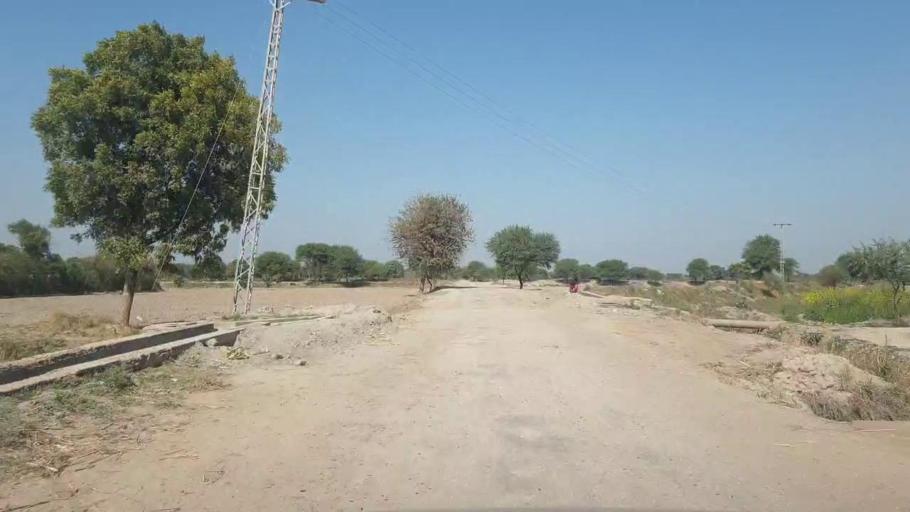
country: PK
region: Sindh
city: Chambar
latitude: 25.2970
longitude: 68.6918
